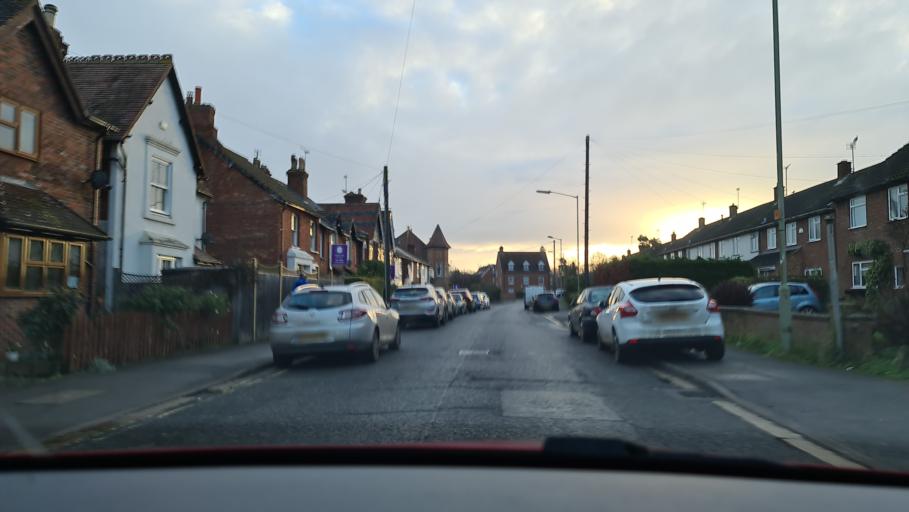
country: GB
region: England
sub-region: Oxfordshire
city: Thame
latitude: 51.7415
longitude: -0.9659
